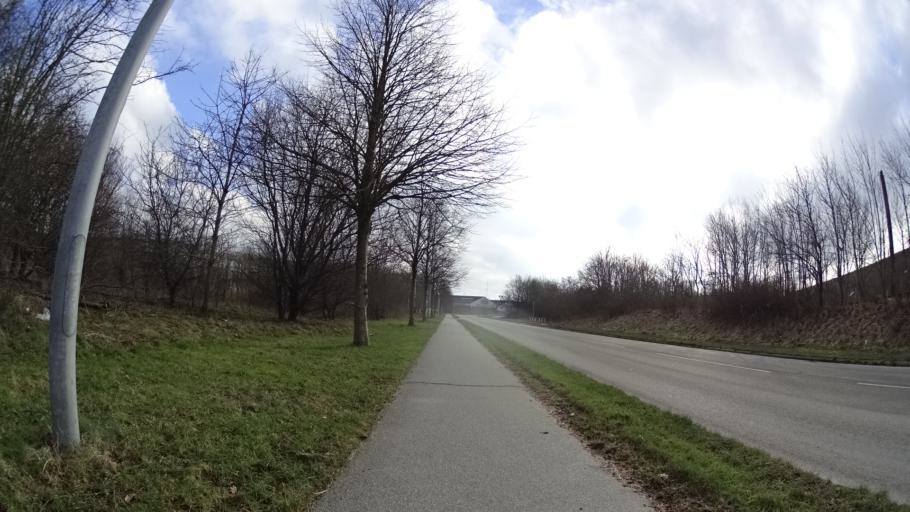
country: DK
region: Central Jutland
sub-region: Arhus Kommune
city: Tranbjerg
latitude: 56.1064
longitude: 10.1172
